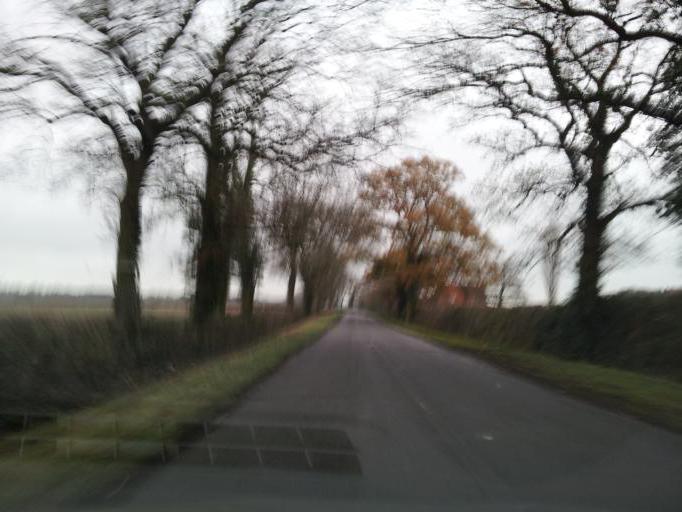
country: GB
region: England
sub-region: Northamptonshire
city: Daventry
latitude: 52.3236
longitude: -1.1895
